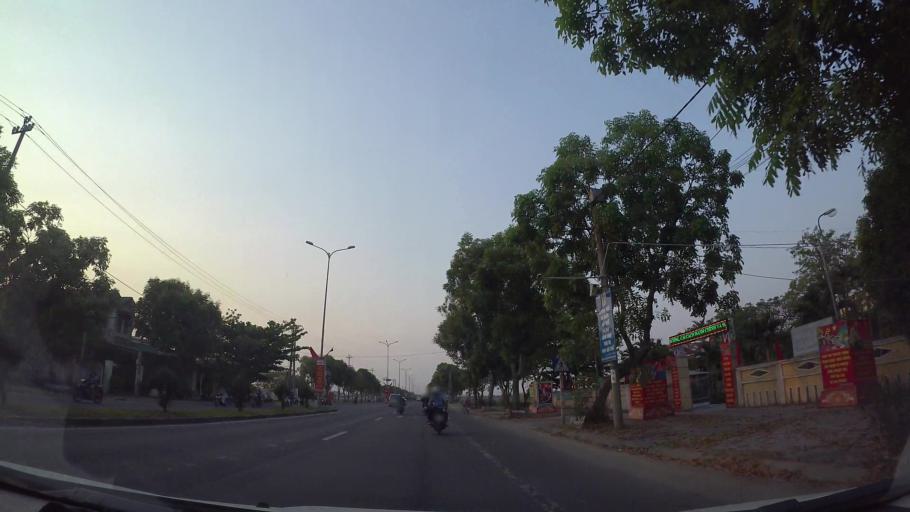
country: VN
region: Da Nang
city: Cam Le
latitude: 15.9586
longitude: 108.2150
